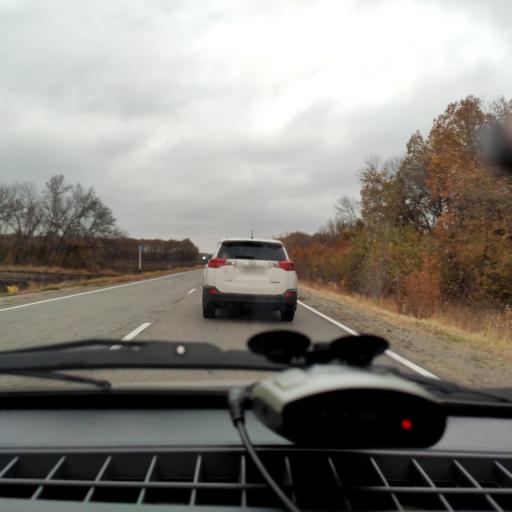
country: RU
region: Voronezj
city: Shilovo
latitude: 51.4165
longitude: 39.0061
